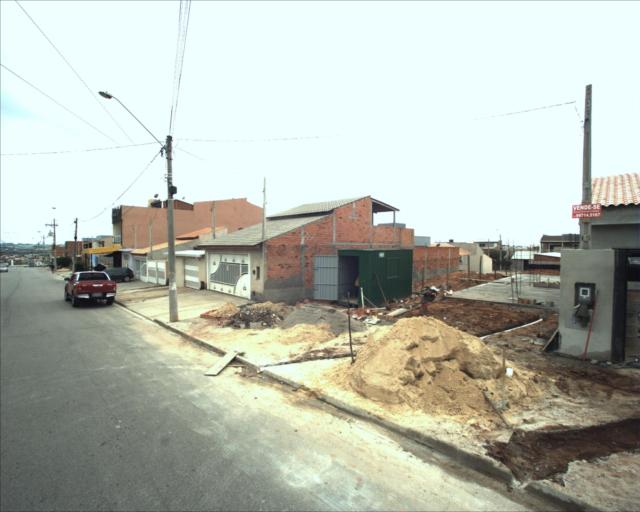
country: BR
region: Sao Paulo
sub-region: Sorocaba
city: Sorocaba
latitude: -23.4408
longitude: -47.4997
